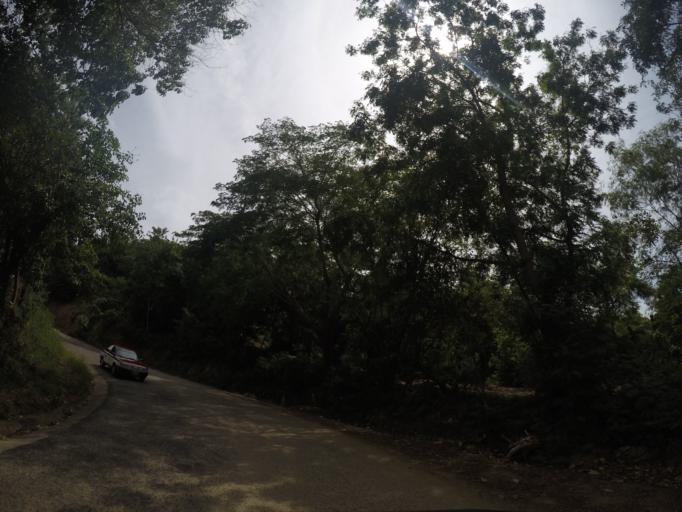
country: MX
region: Oaxaca
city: Santa Maria Tonameca
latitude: 15.6676
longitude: -96.5258
